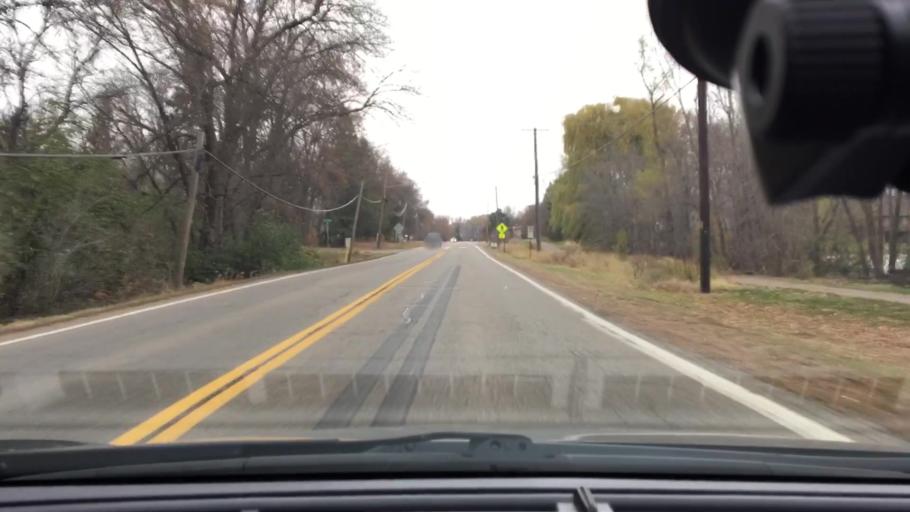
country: US
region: Minnesota
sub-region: Hennepin County
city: Corcoran
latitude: 45.1039
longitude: -93.5120
